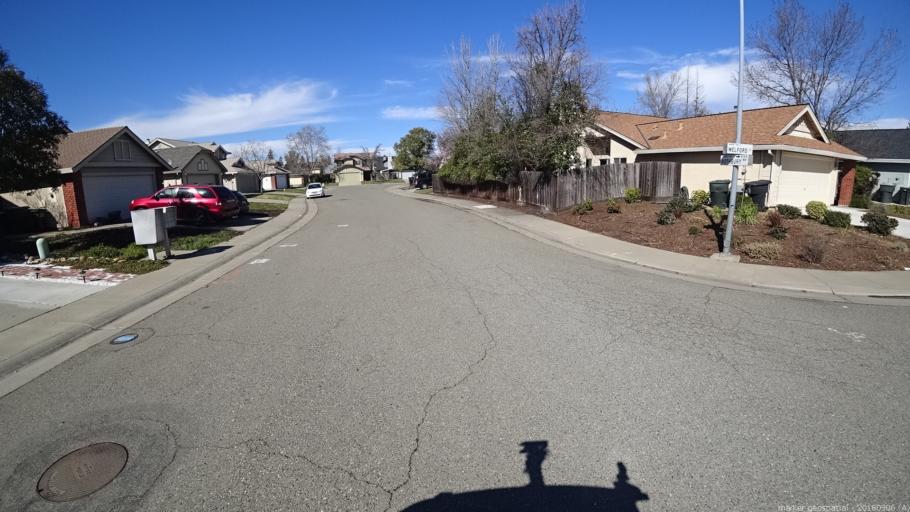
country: US
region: California
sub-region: Sacramento County
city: Vineyard
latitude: 38.4608
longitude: -121.3556
